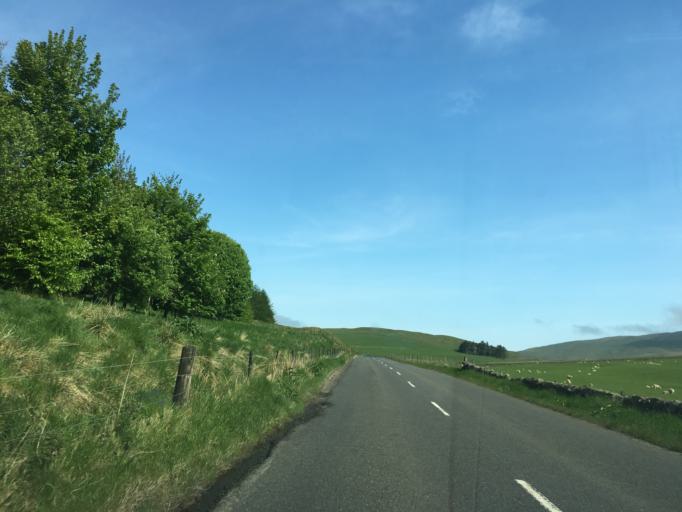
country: GB
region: Scotland
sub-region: South Lanarkshire
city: Biggar
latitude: 55.6380
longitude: -3.4257
